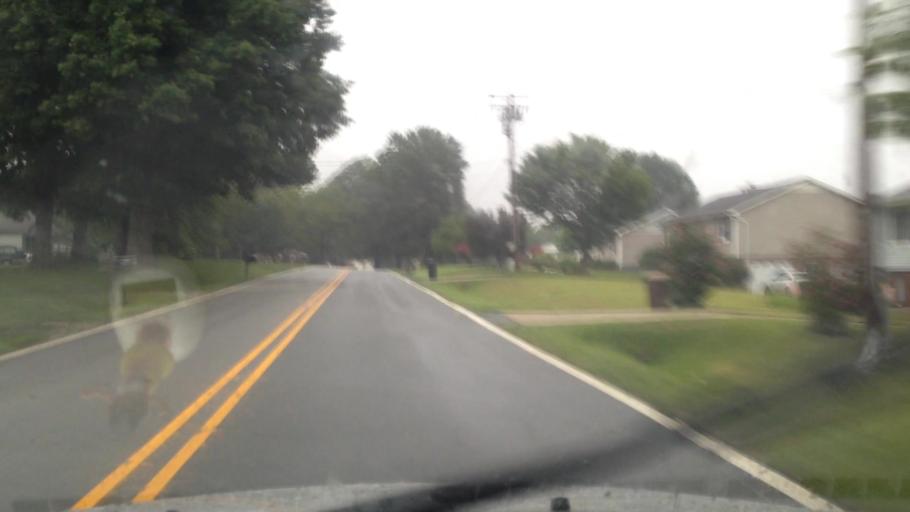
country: US
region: North Carolina
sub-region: Forsyth County
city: Walkertown
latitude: 36.1532
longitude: -80.1265
